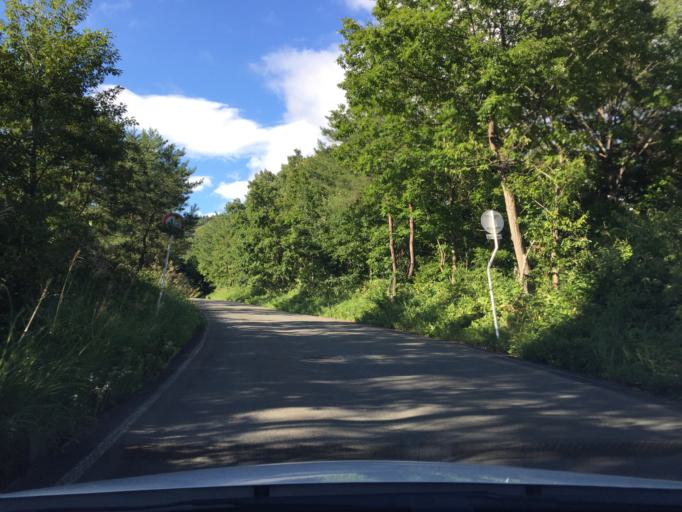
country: JP
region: Yamagata
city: Yonezawa
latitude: 37.8917
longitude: 140.1934
